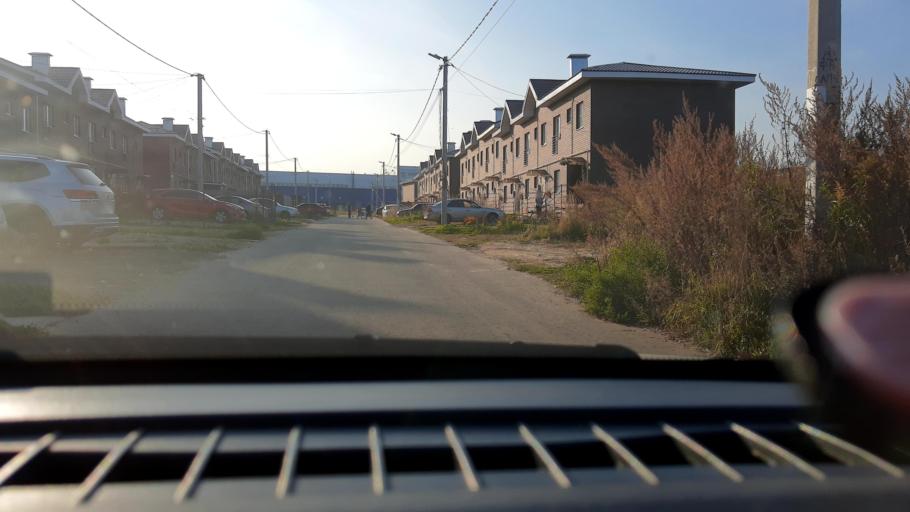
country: RU
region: Nizjnij Novgorod
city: Afonino
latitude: 56.2144
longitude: 44.0871
